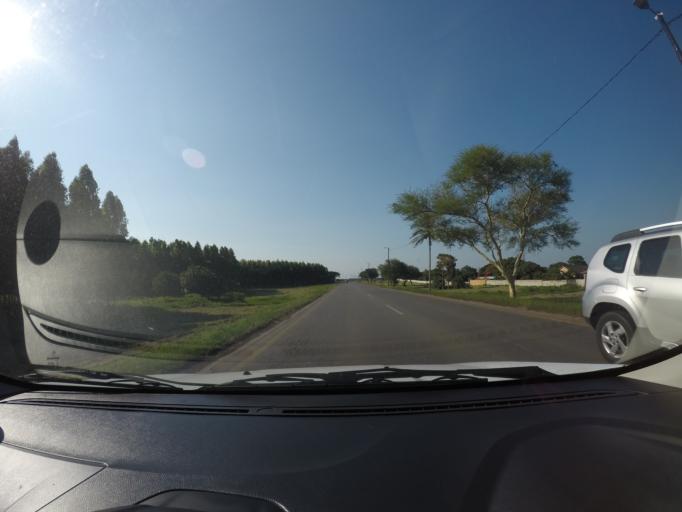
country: ZA
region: KwaZulu-Natal
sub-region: uThungulu District Municipality
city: Richards Bay
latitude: -28.7181
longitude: 32.0322
